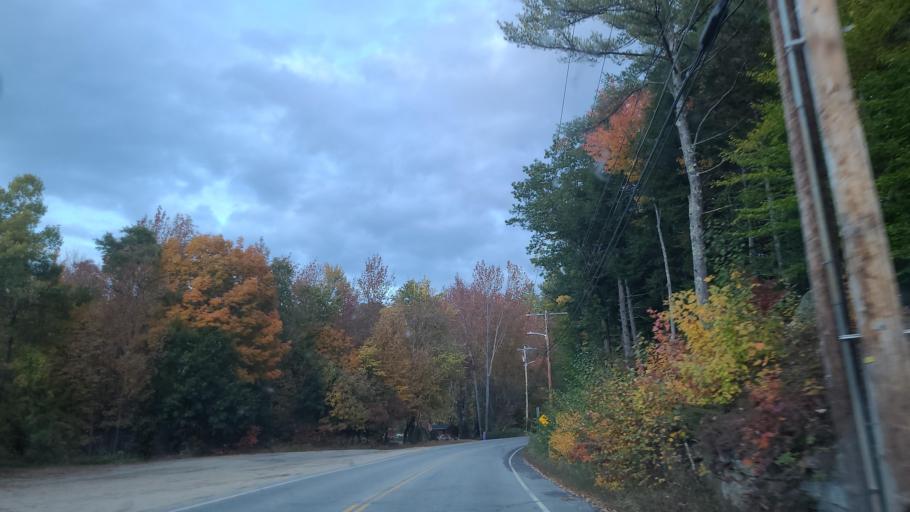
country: US
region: New Hampshire
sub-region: Carroll County
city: North Conway
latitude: 44.1475
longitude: -71.1807
